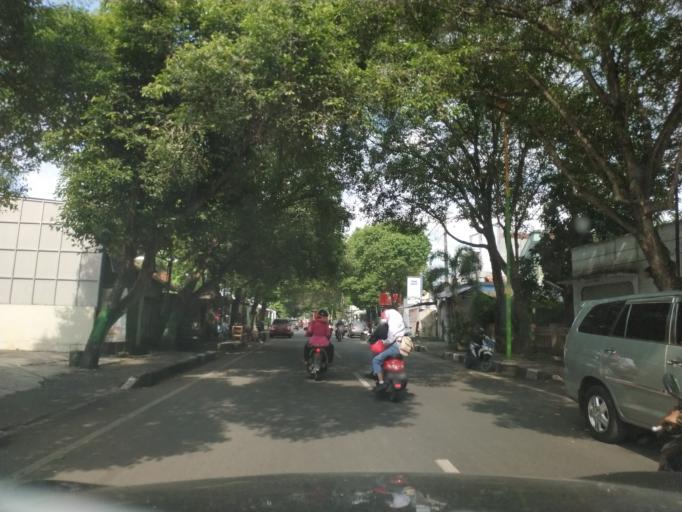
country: ID
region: Central Java
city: Pati
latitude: -6.7555
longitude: 111.0379
